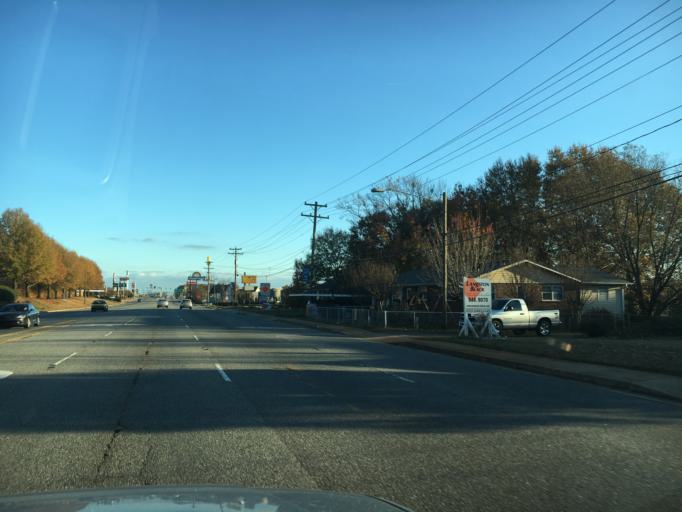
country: US
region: South Carolina
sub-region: Spartanburg County
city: Lyman
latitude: 34.9192
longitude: -82.1136
